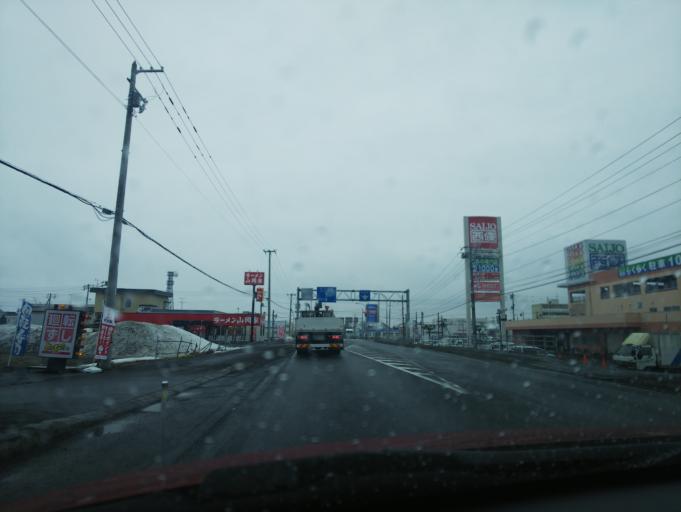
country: JP
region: Hokkaido
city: Nayoro
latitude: 44.1651
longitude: 142.3956
